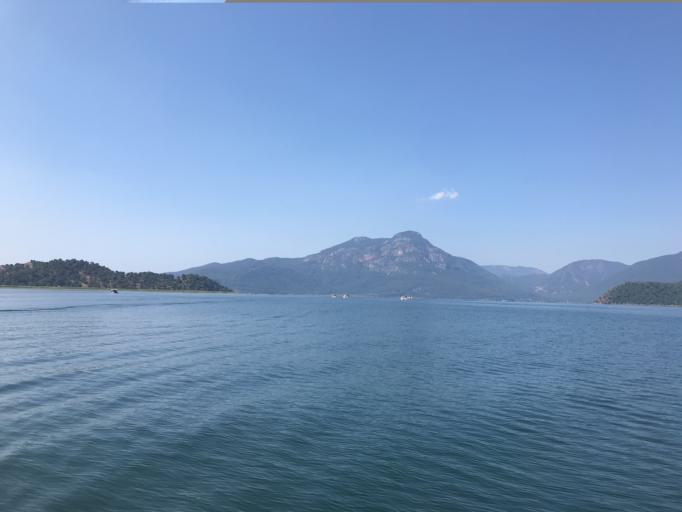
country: TR
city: Dalyan
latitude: 36.9099
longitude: 28.6524
